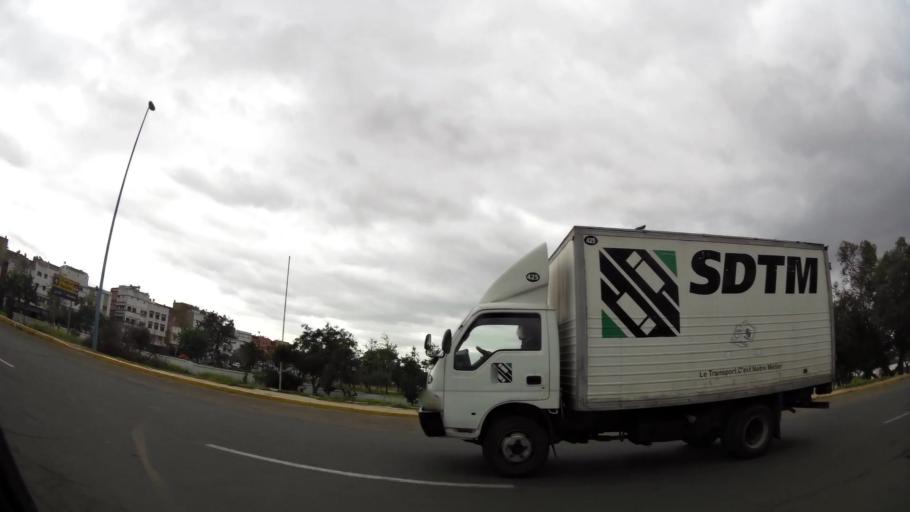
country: MA
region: Grand Casablanca
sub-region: Casablanca
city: Casablanca
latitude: 33.5670
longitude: -7.5748
